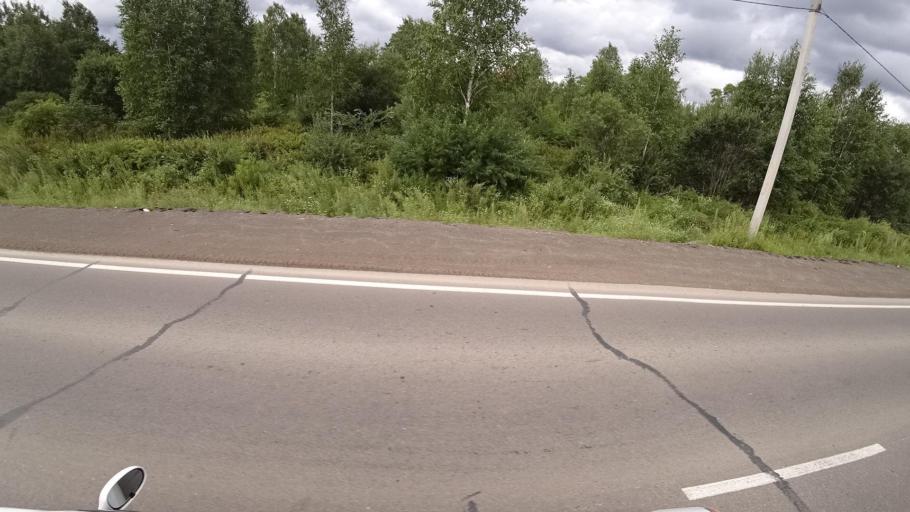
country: RU
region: Khabarovsk Krai
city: Solnechnyy
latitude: 50.5858
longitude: 137.0252
